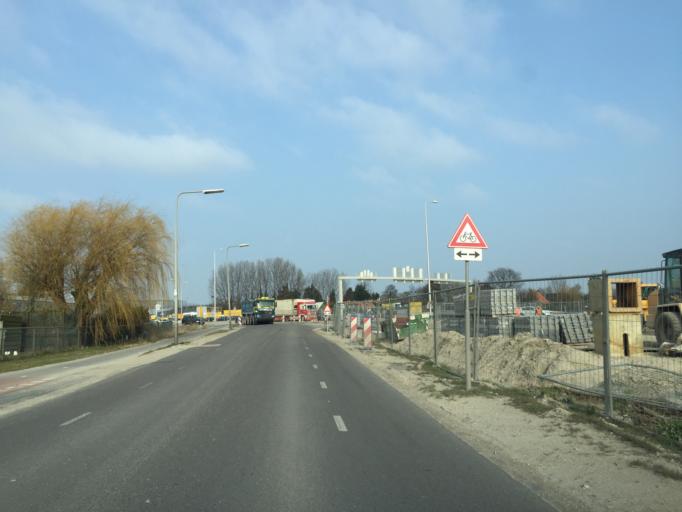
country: NL
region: South Holland
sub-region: Gemeente Westland
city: Maasdijk
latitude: 51.9729
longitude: 4.2148
